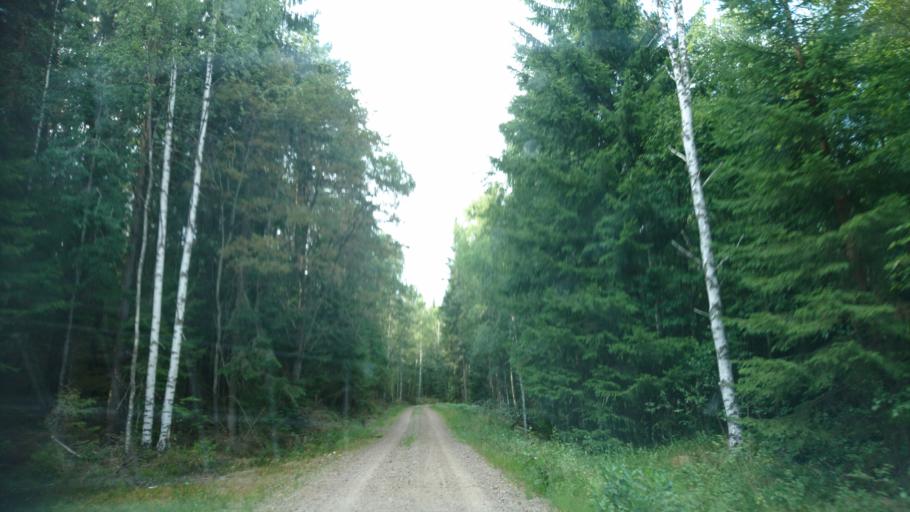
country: SE
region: Vaermland
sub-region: Kristinehamns Kommun
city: Bjorneborg
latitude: 59.3062
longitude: 14.3109
